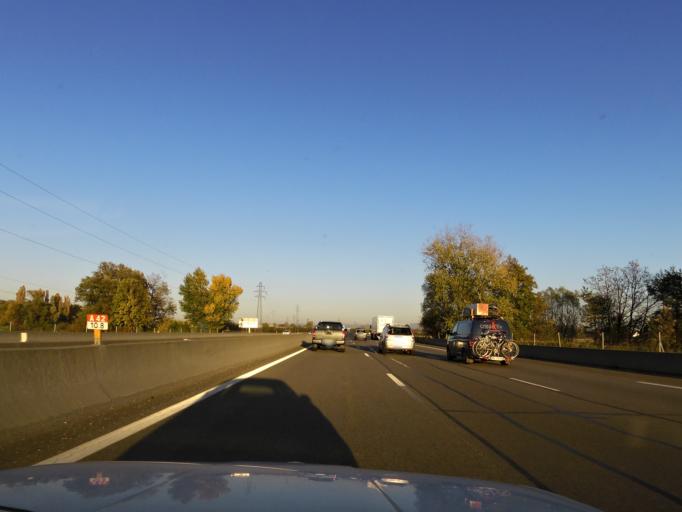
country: FR
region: Rhone-Alpes
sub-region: Departement de l'Ain
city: Beynost
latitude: 45.8243
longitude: 5.0060
